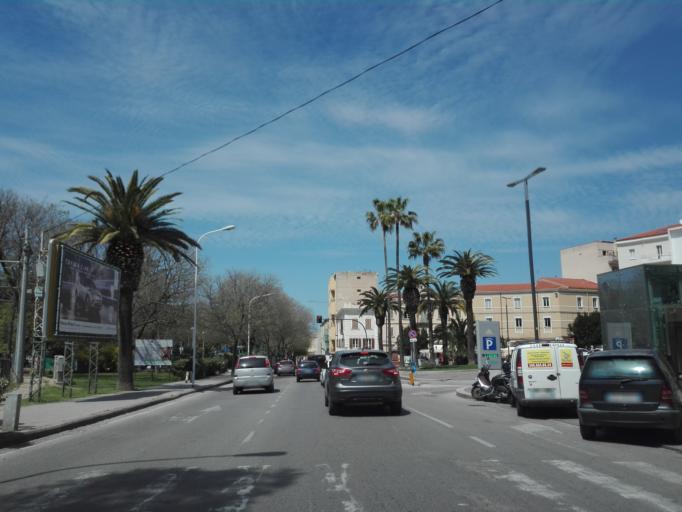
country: IT
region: Sardinia
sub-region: Provincia di Sassari
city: Sassari
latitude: 40.7229
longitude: 8.5618
